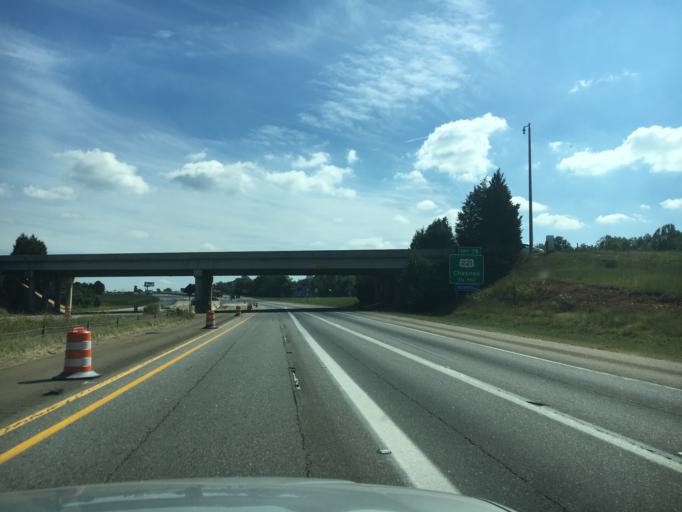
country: US
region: South Carolina
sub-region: Spartanburg County
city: Valley Falls
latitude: 35.0111
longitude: -81.9158
